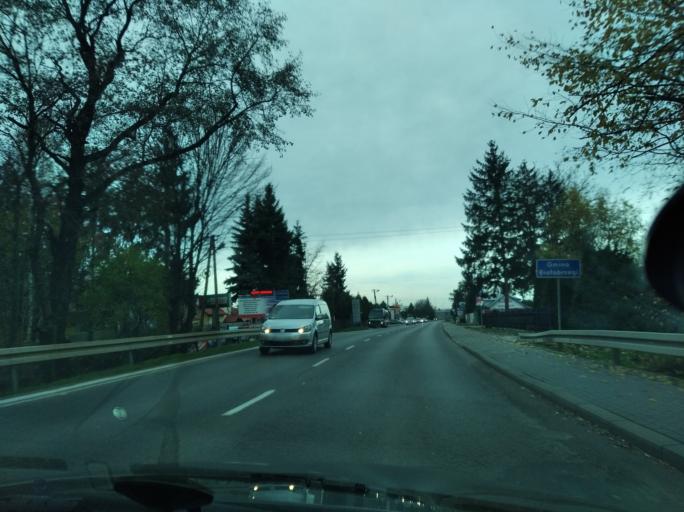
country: PL
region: Subcarpathian Voivodeship
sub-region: Powiat lancucki
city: Lancut
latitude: 50.0949
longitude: 22.2312
